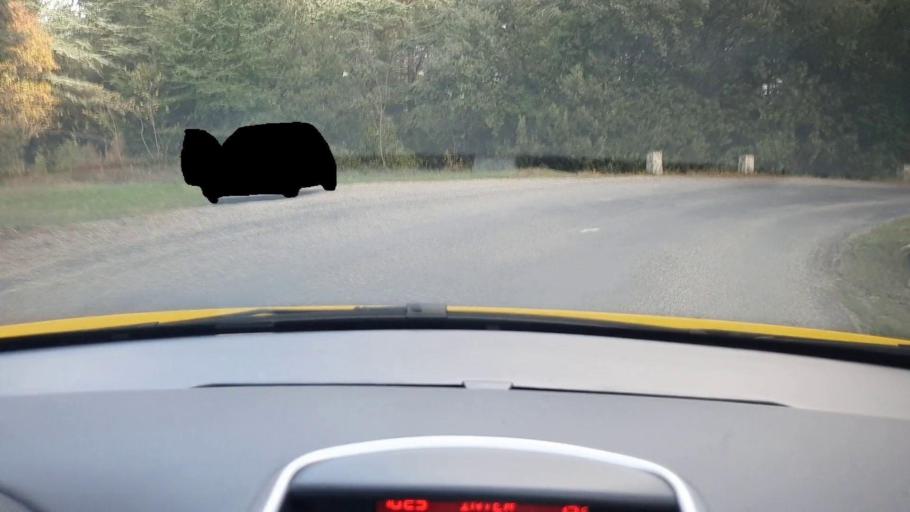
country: FR
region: Languedoc-Roussillon
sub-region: Departement du Gard
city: Lasalle
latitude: 44.0312
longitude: 3.8339
